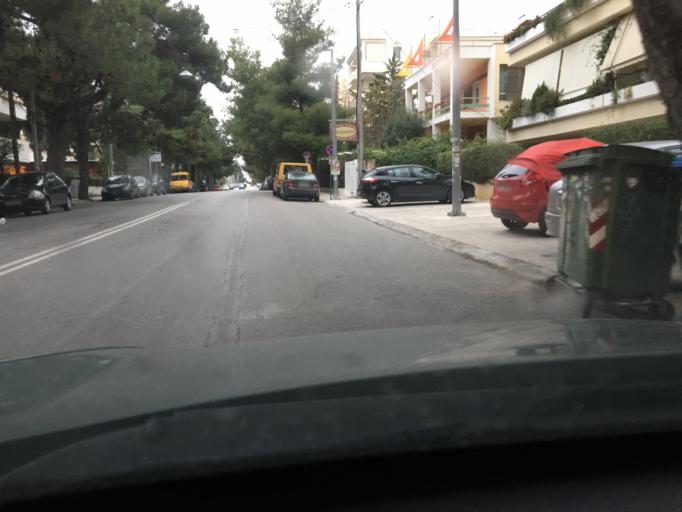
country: GR
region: Attica
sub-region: Nomarchia Athinas
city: Vrilissia
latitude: 38.0314
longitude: 23.8279
